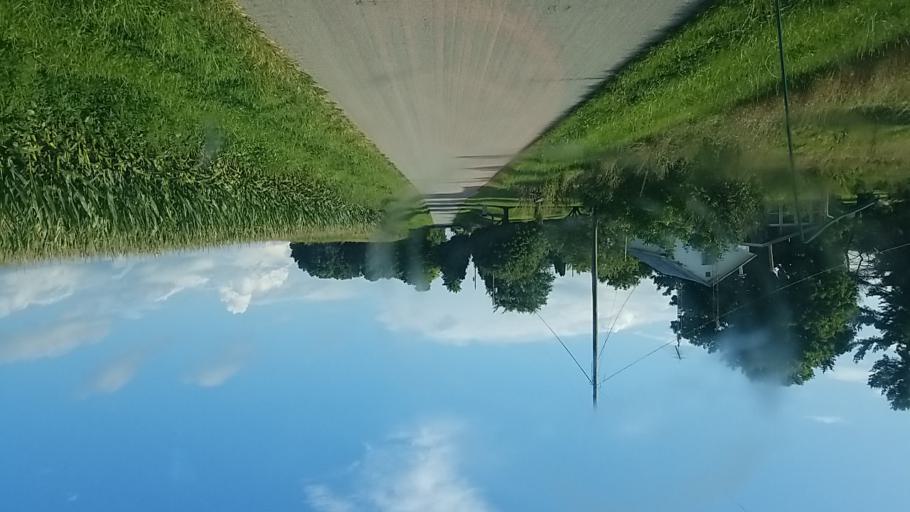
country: US
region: Ohio
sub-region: Wyandot County
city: Upper Sandusky
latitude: 40.8198
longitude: -83.1601
